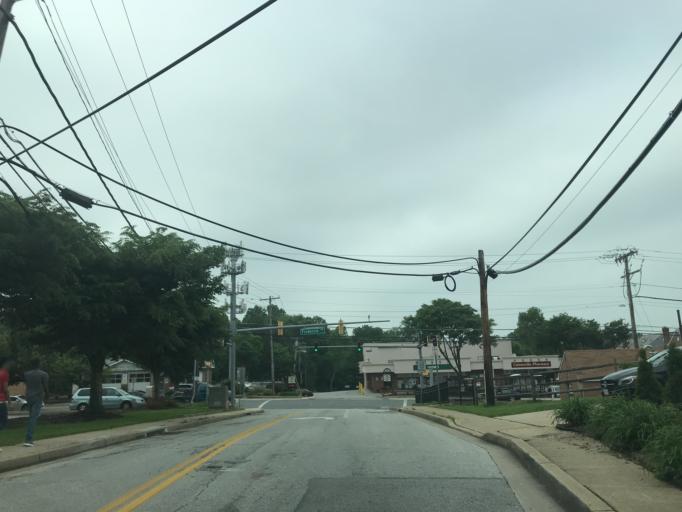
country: US
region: Maryland
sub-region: Baltimore County
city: Charlestown
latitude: 39.2751
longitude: -76.7169
